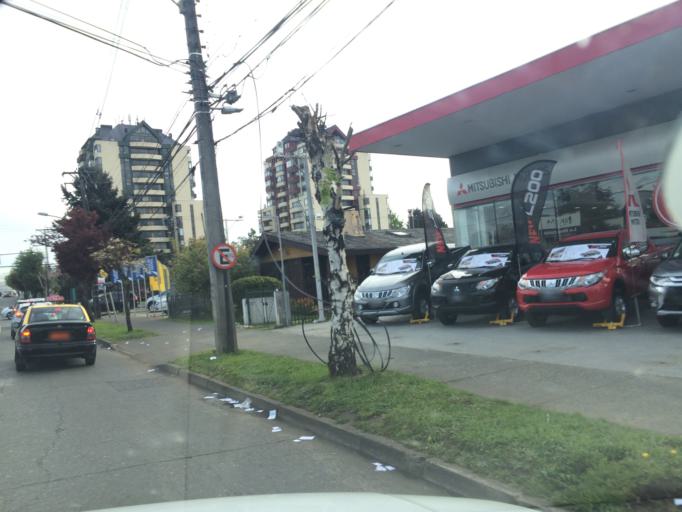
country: CL
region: Araucania
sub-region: Provincia de Cautin
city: Temuco
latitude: -38.7386
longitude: -72.6177
